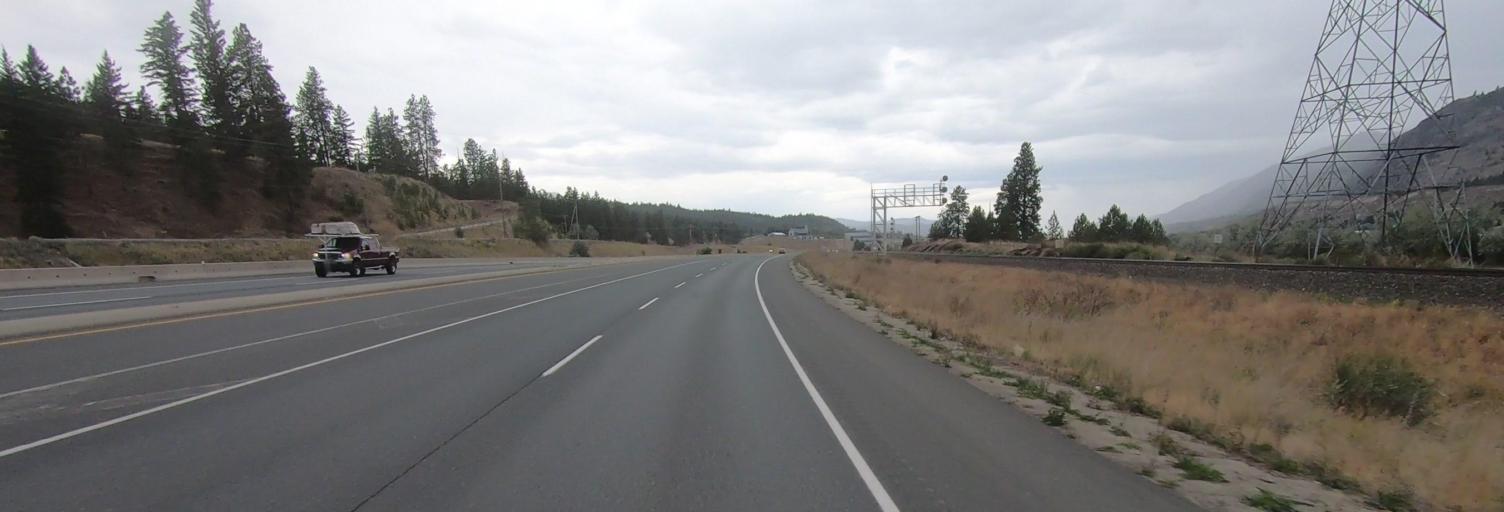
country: CA
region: British Columbia
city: Chase
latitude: 50.6459
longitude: -119.9074
